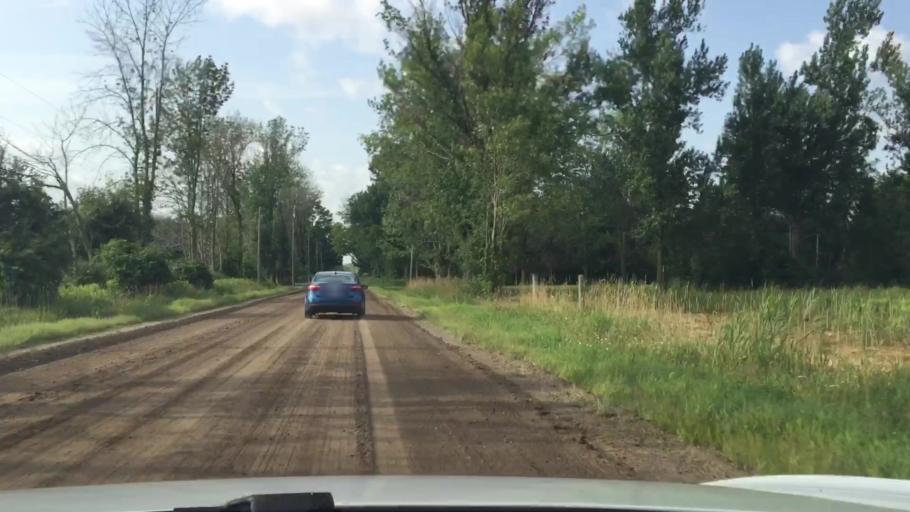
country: CA
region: Ontario
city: Oshawa
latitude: 43.9281
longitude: -78.7419
